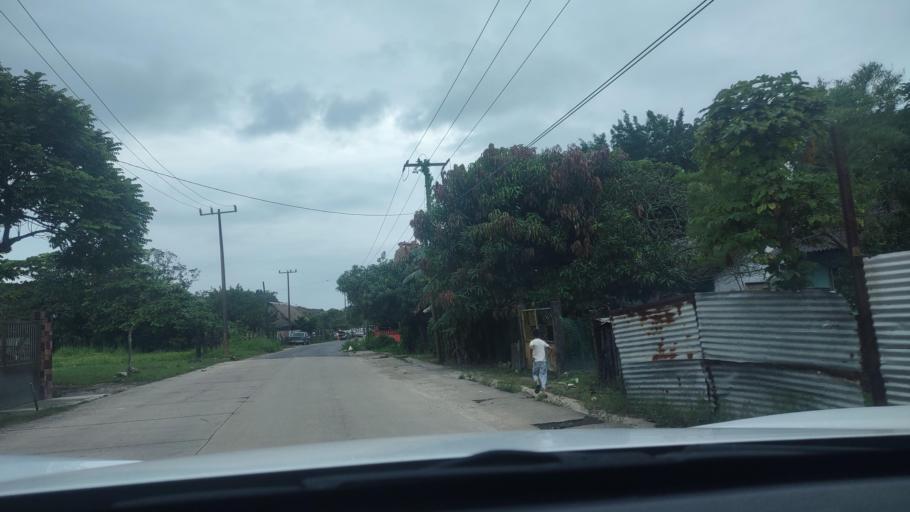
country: MX
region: Veracruz
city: Villa Nanchital
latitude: 18.0454
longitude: -94.3529
